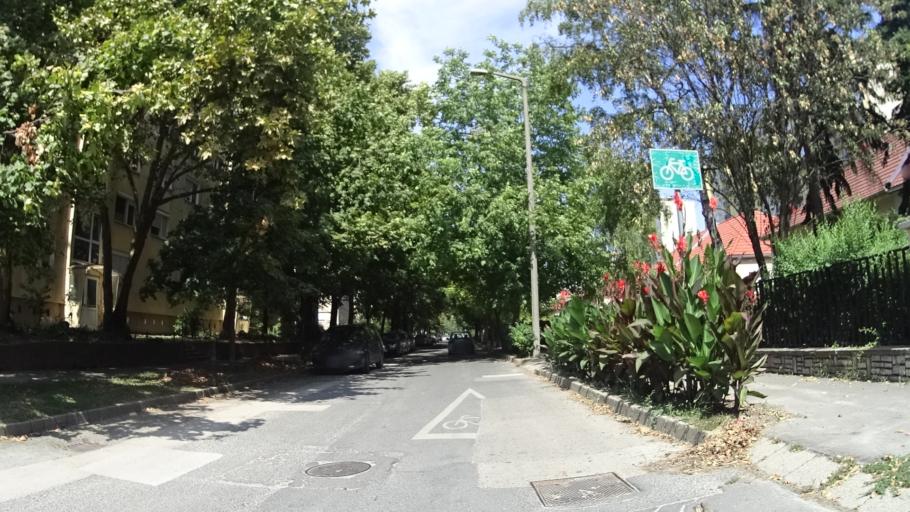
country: HU
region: Fejer
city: Szekesfehervar
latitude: 47.1811
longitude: 18.4143
